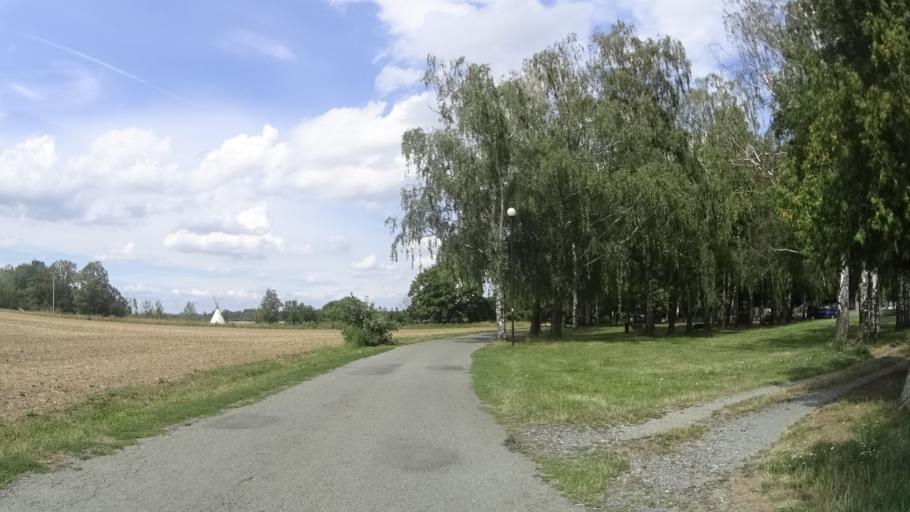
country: CZ
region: Olomoucky
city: Horka nad Moravou
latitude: 49.6424
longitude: 17.1972
